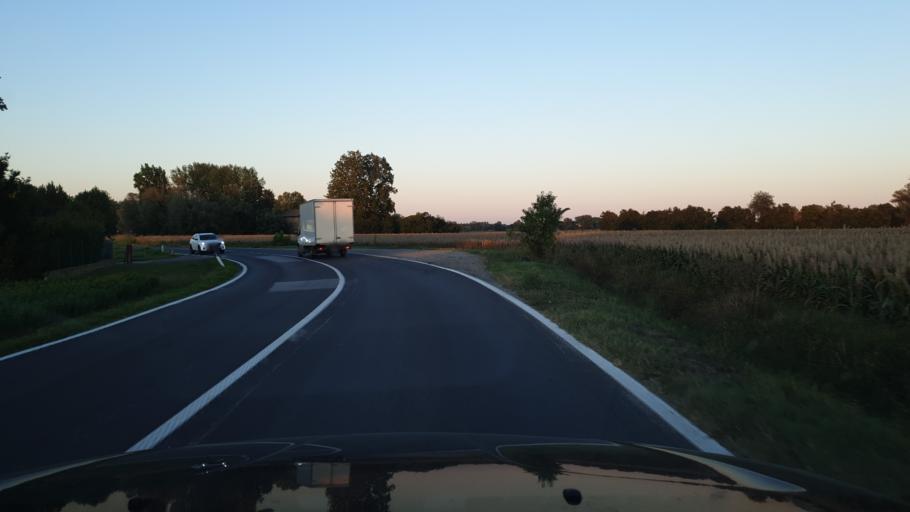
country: IT
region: Emilia-Romagna
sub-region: Provincia di Bologna
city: Granarolo dell'Emilia e Viadagola
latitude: 44.5762
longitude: 11.4108
